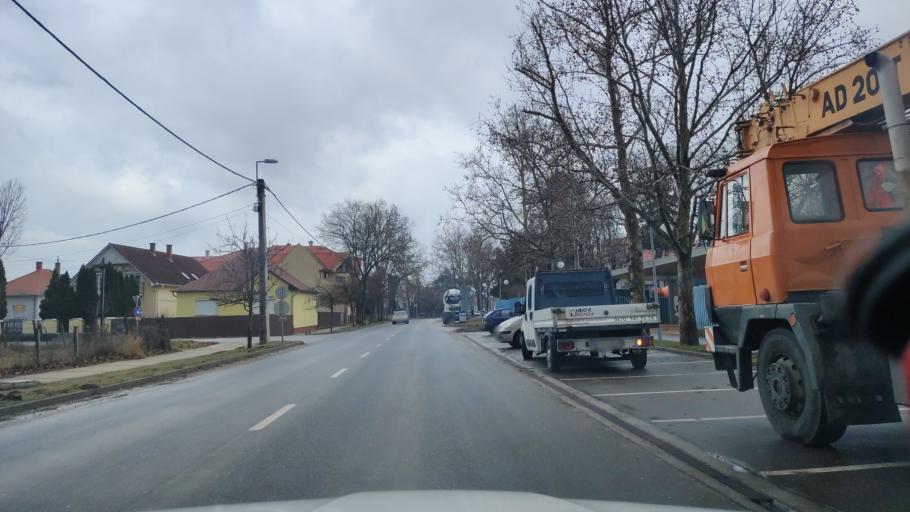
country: HU
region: Hajdu-Bihar
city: Hajduszoboszlo
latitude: 47.4525
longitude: 21.3947
